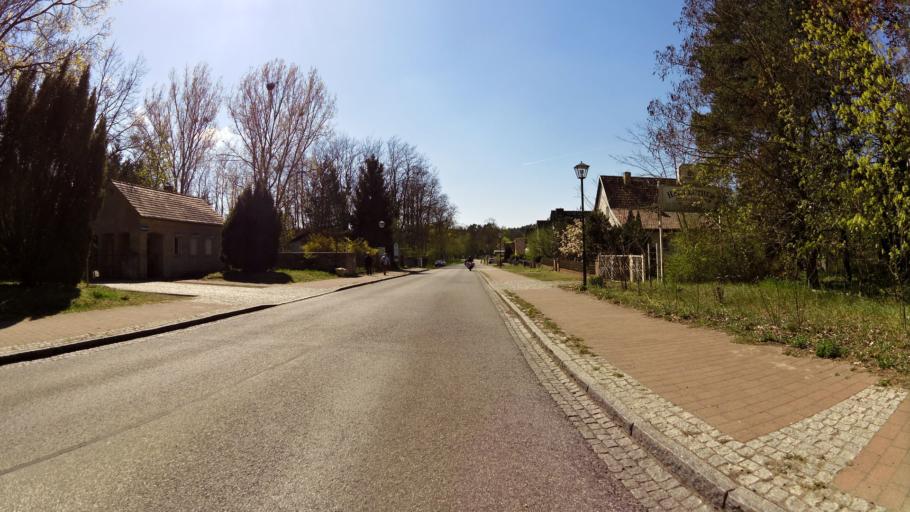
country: DE
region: Brandenburg
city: Waldsieversdorf
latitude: 52.5576
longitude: 14.0682
